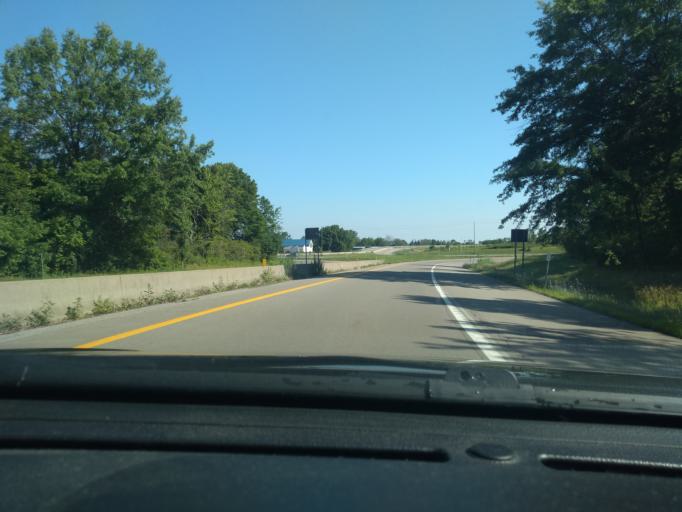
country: US
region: New York
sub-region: Erie County
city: Orchard Park
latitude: 42.7875
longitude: -78.7770
